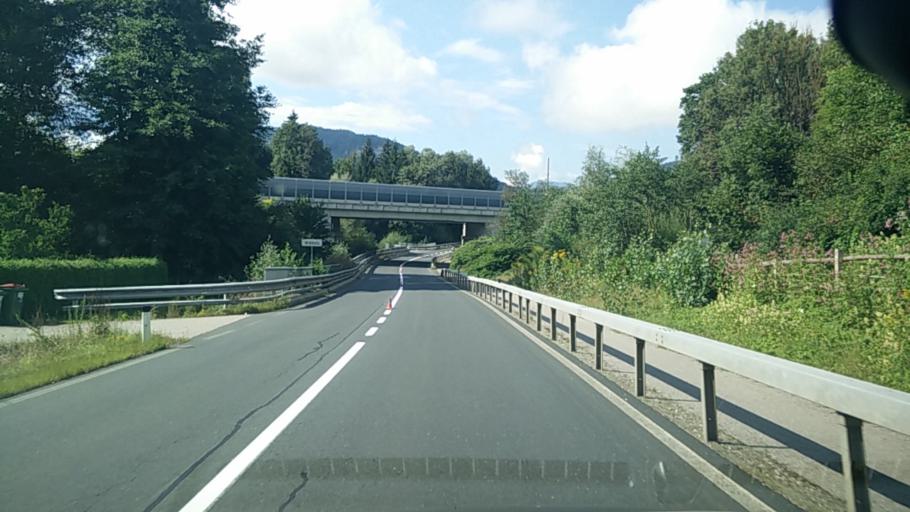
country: AT
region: Carinthia
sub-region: Politischer Bezirk Klagenfurt Land
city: Grafenstein
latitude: 46.6144
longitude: 14.5034
